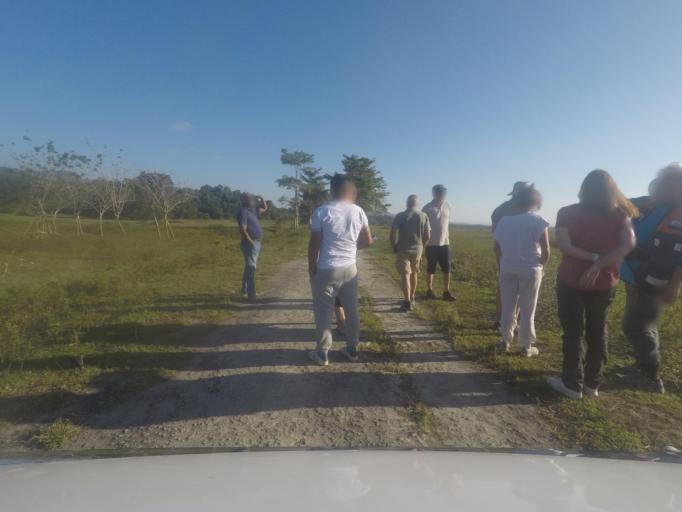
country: TL
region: Lautem
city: Lospalos
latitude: -8.4373
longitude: 127.1842
